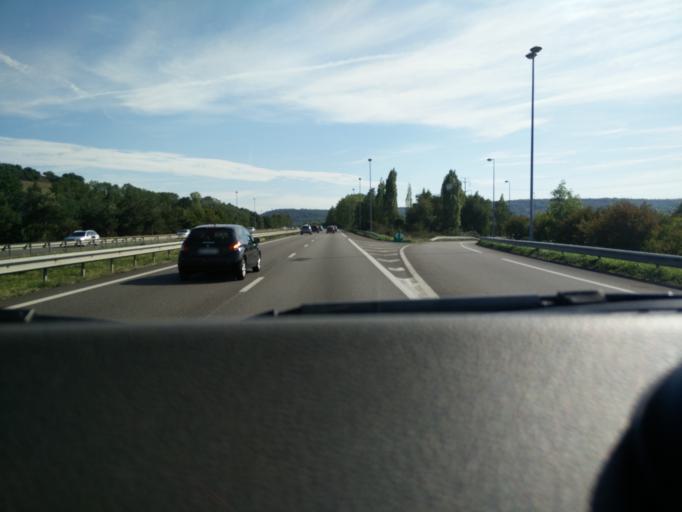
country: FR
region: Lorraine
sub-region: Departement de Meurthe-et-Moselle
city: Custines
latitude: 48.7778
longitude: 6.1445
